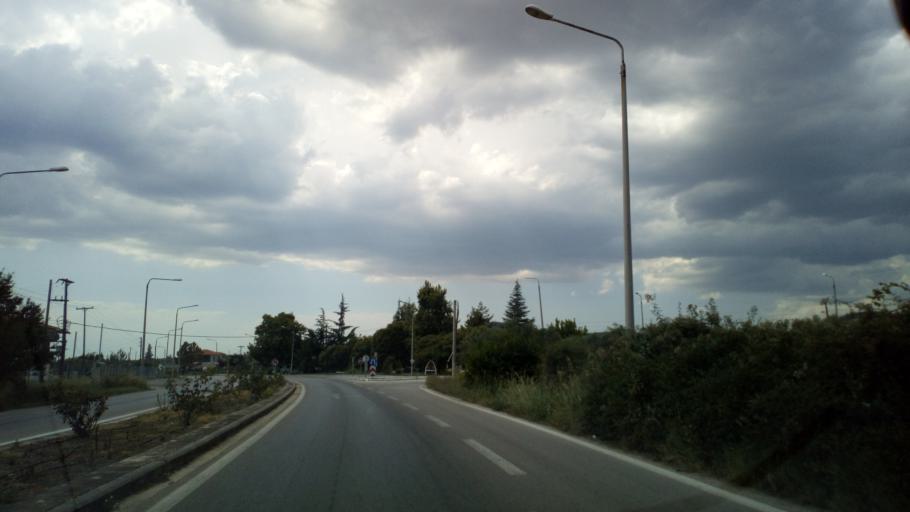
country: GR
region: Central Macedonia
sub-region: Nomos Chalkidikis
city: Ormylia
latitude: 40.2628
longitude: 23.5171
